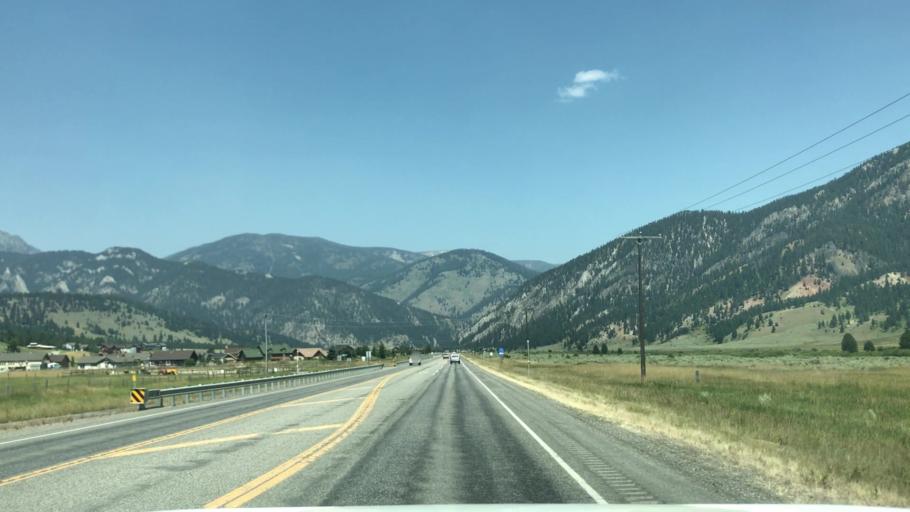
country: US
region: Montana
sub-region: Gallatin County
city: Big Sky
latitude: 45.2354
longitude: -111.2508
